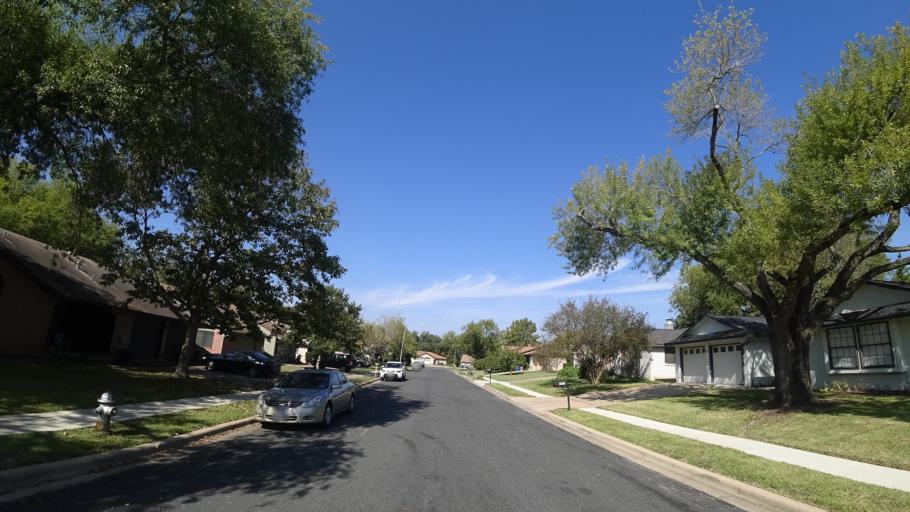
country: US
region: Texas
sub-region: Travis County
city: Shady Hollow
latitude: 30.2137
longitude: -97.8190
